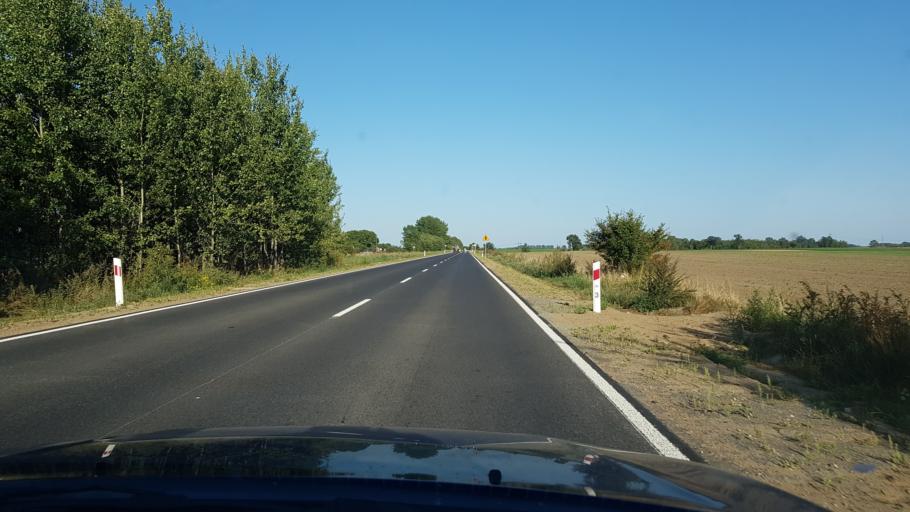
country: PL
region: West Pomeranian Voivodeship
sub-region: Powiat goleniowski
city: Maszewo
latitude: 53.4338
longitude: 15.0799
